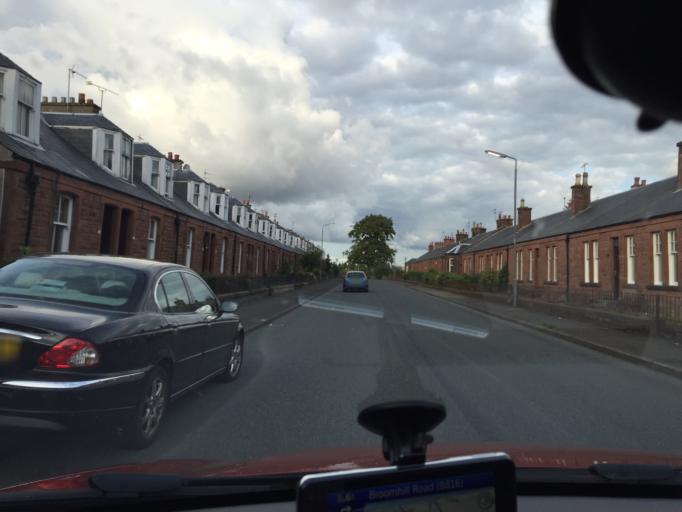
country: GB
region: Scotland
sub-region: Falkirk
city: Bonnybridge
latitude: 55.9868
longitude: -3.9225
